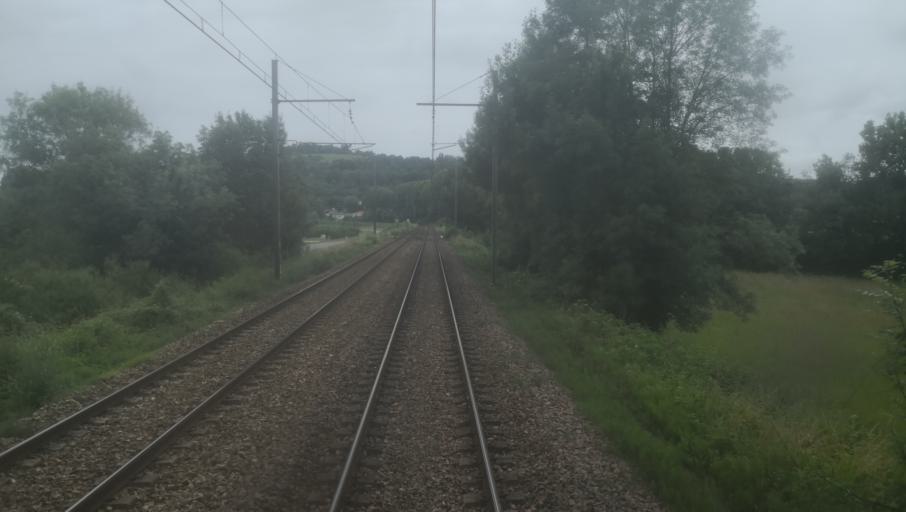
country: FR
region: Aquitaine
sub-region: Departement du Lot-et-Garonne
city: Port-Sainte-Marie
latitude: 44.2472
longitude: 0.4137
